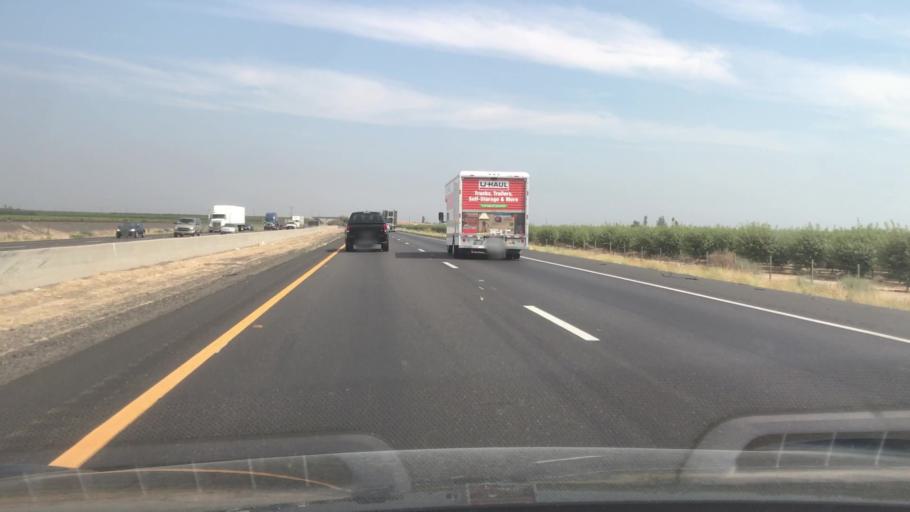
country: US
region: California
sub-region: Madera County
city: Parksdale
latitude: 36.9179
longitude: -120.0149
